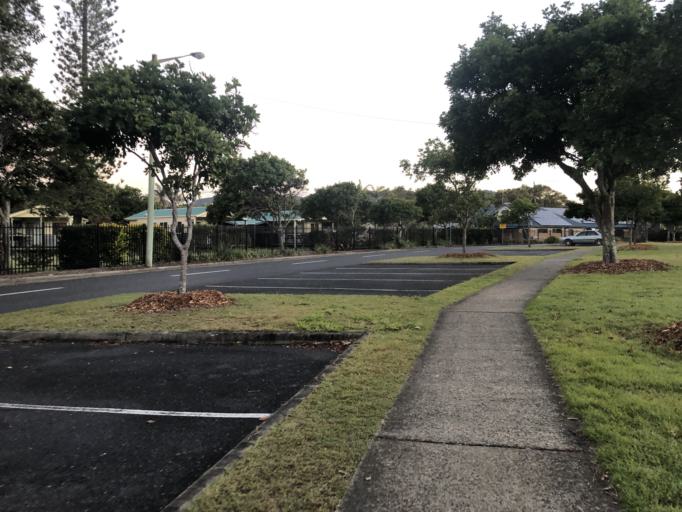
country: AU
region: New South Wales
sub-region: Coffs Harbour
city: Coffs Harbour
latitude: -30.2935
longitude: 153.1383
